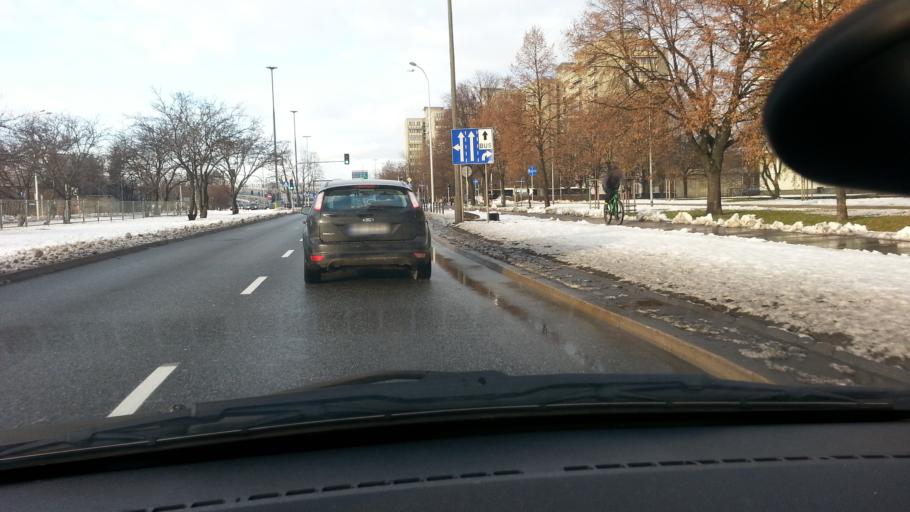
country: PL
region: Masovian Voivodeship
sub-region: Warszawa
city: Targowek
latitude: 52.2903
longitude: 21.0192
